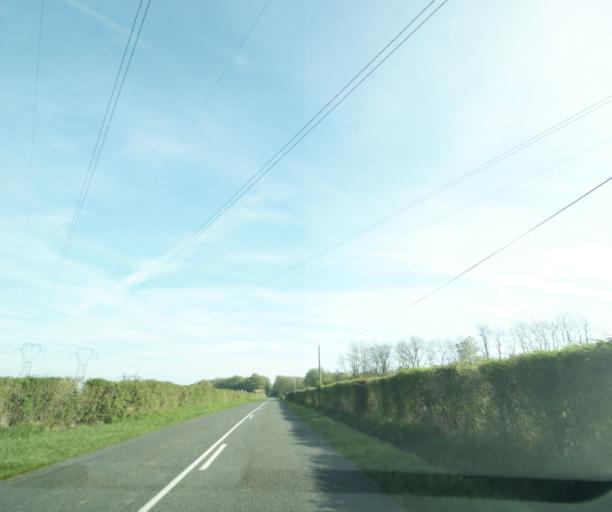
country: FR
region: Ile-de-France
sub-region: Departement de Seine-et-Marne
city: Vernou-la-Celle-sur-Seine
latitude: 48.4398
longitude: 2.8560
